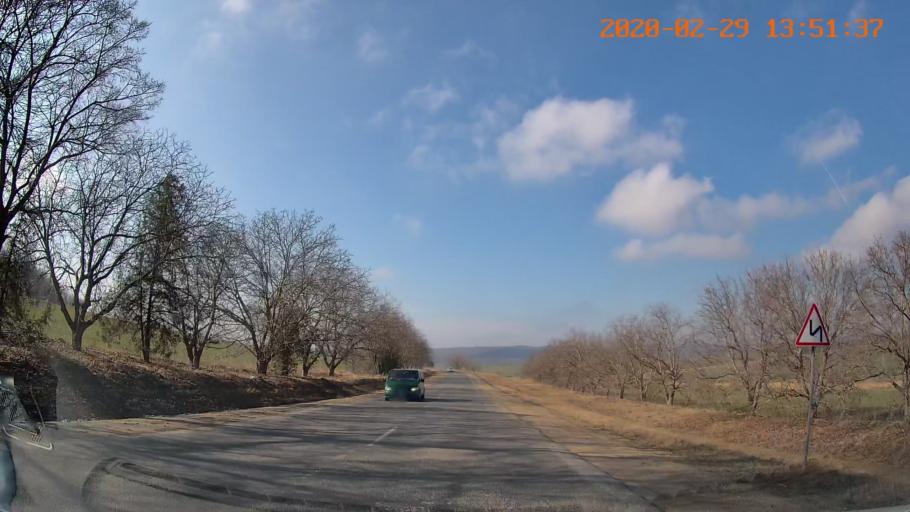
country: MD
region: Floresti
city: Leninskiy
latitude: 47.8430
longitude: 28.4604
